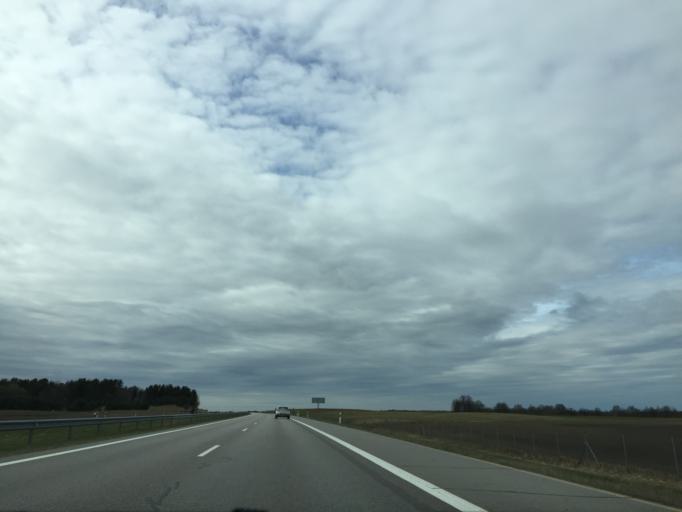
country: LT
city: Silale
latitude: 55.5951
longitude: 22.1280
